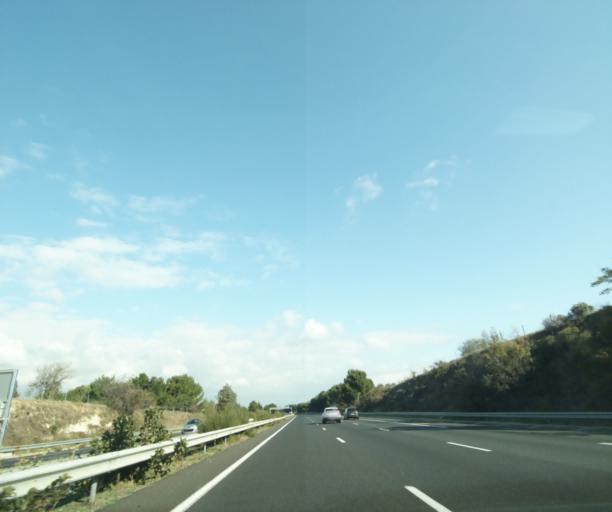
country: FR
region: Languedoc-Roussillon
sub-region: Departement de l'Aude
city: Fleury
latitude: 43.2305
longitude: 3.1193
